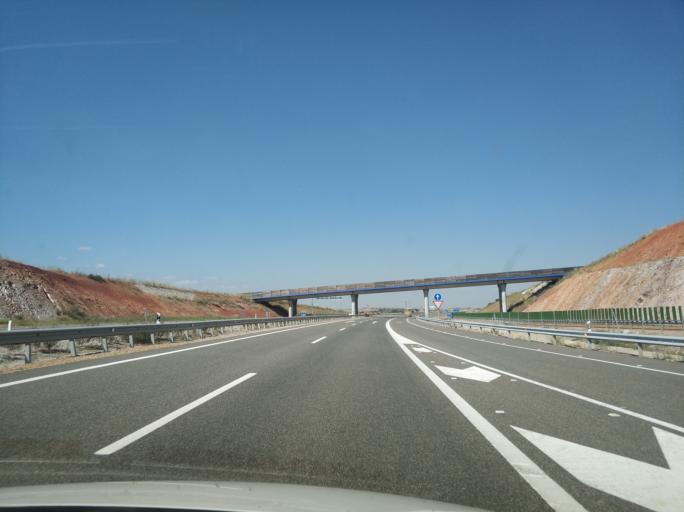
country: ES
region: Castille and Leon
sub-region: Provincia de Zamora
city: Montamarta
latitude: 41.6903
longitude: -5.8023
